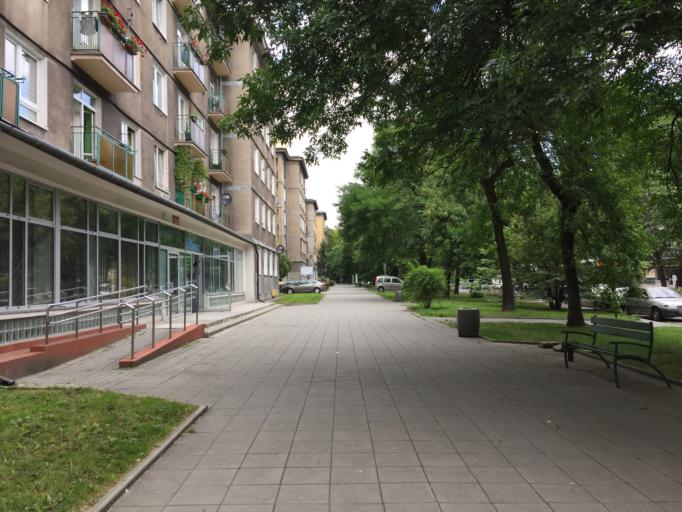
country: PL
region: Lesser Poland Voivodeship
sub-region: Powiat wielicki
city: Kokotow
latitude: 50.0772
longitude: 20.0388
